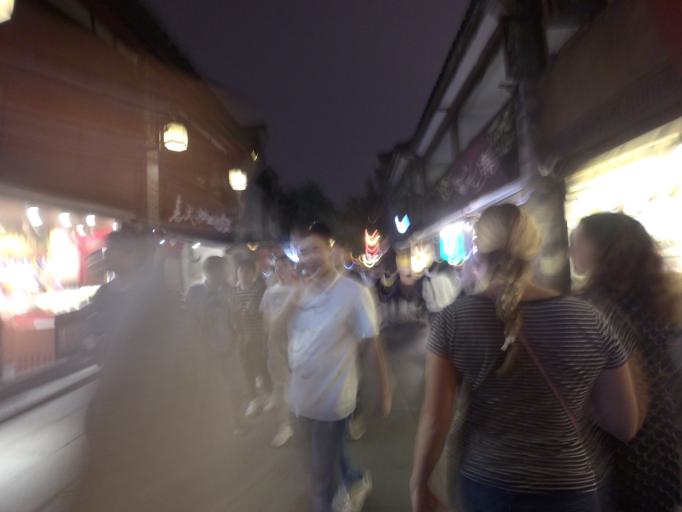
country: CN
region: Sichuan
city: Chengdu
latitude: 30.6476
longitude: 104.0473
